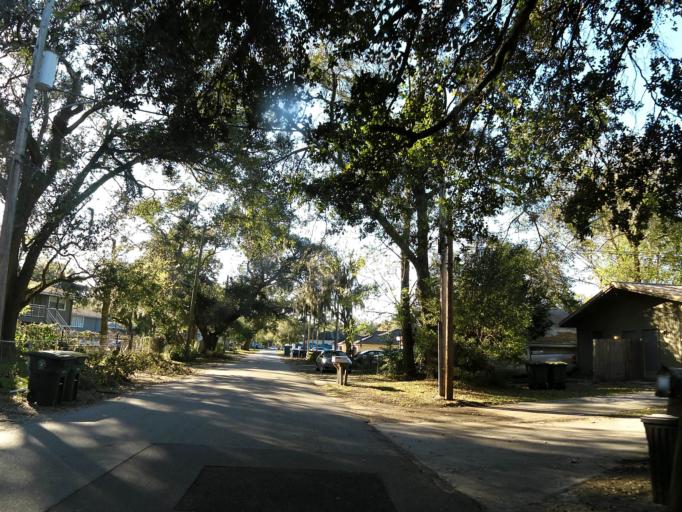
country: US
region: Florida
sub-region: Duval County
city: Jacksonville
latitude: 30.2586
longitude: -81.6238
